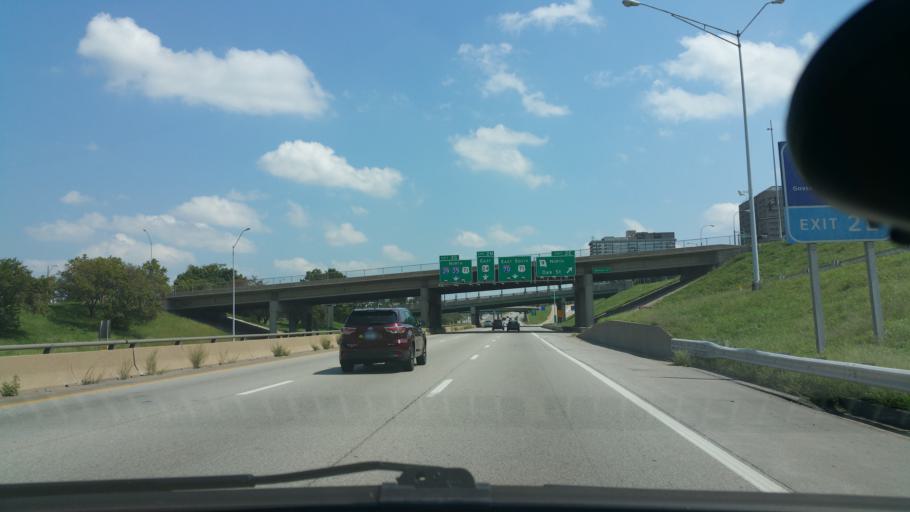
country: US
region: Missouri
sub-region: Jackson County
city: Kansas City
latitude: 39.1067
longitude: -94.5829
